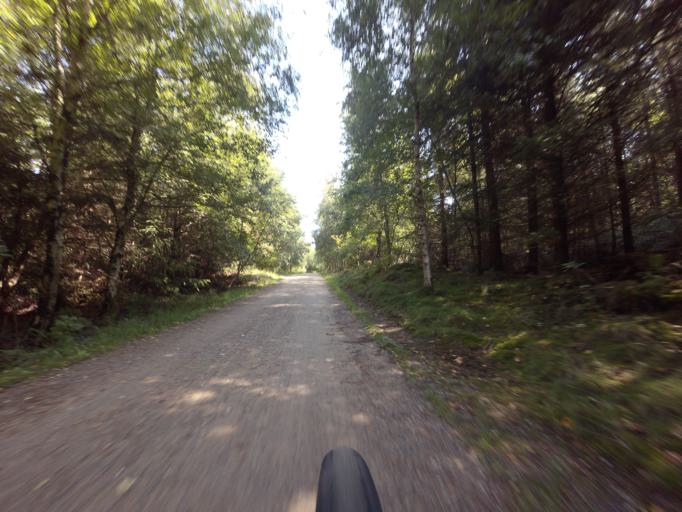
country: DK
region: North Denmark
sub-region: Hjorring Kommune
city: Hirtshals
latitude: 57.5836
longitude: 10.0696
